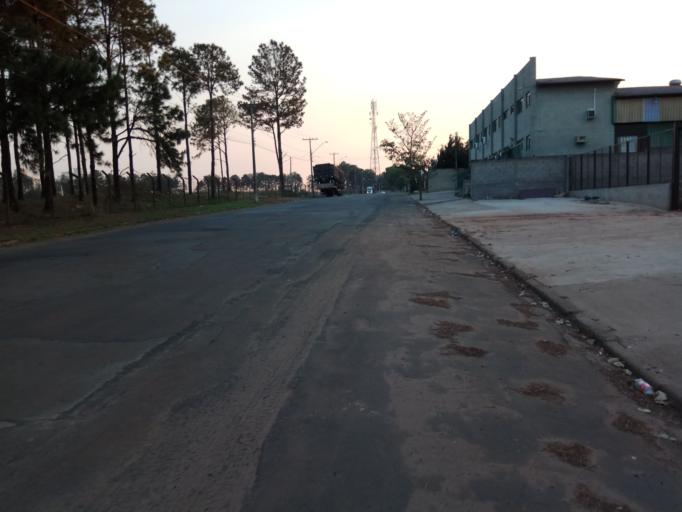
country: BR
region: Sao Paulo
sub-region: Piracicaba
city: Piracicaba
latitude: -22.7347
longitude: -47.5947
